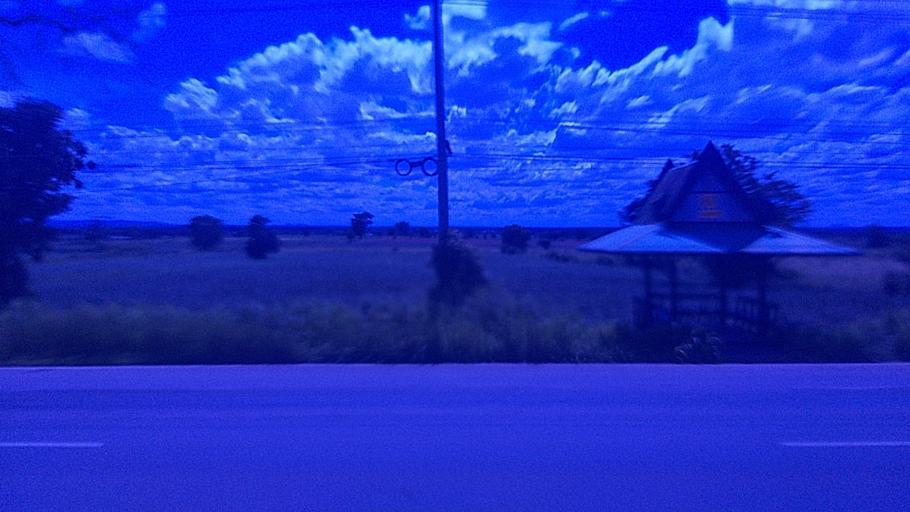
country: TH
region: Nakhon Ratchasima
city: Dan Khun Thot
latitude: 15.1276
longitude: 101.7264
